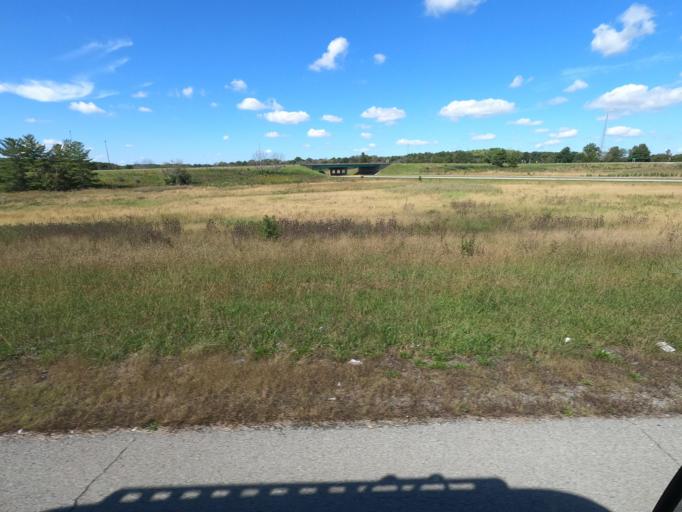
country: US
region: Illinois
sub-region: Jefferson County
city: Mount Vernon
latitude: 38.3608
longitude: -89.0327
